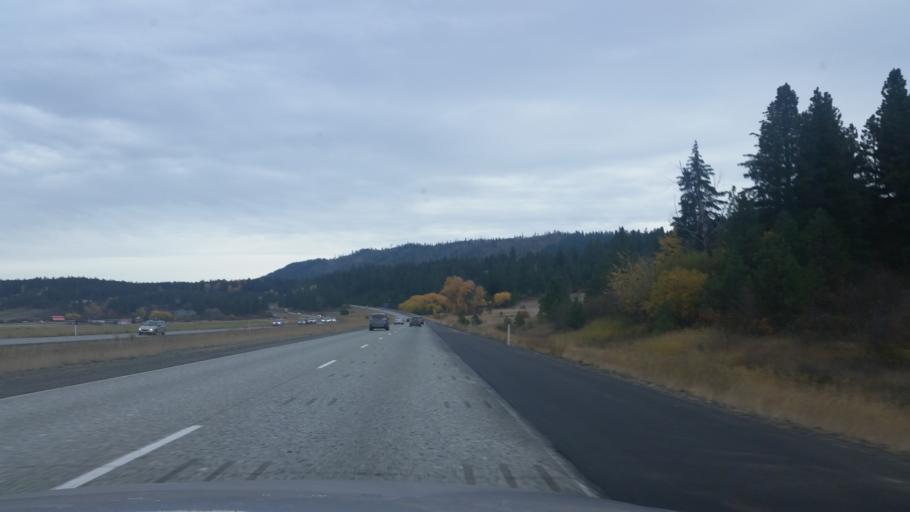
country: US
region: Washington
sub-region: Kittitas County
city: Cle Elum
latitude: 47.1672
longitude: -120.8794
